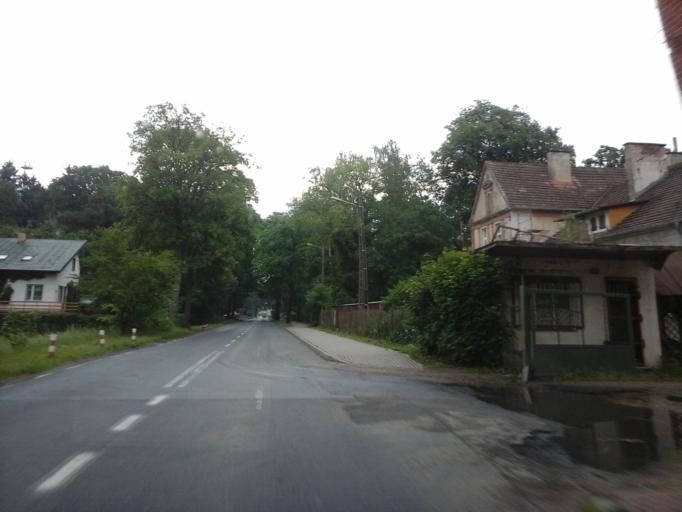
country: PL
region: West Pomeranian Voivodeship
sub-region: Powiat choszczenski
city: Drawno
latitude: 53.2115
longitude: 15.7415
